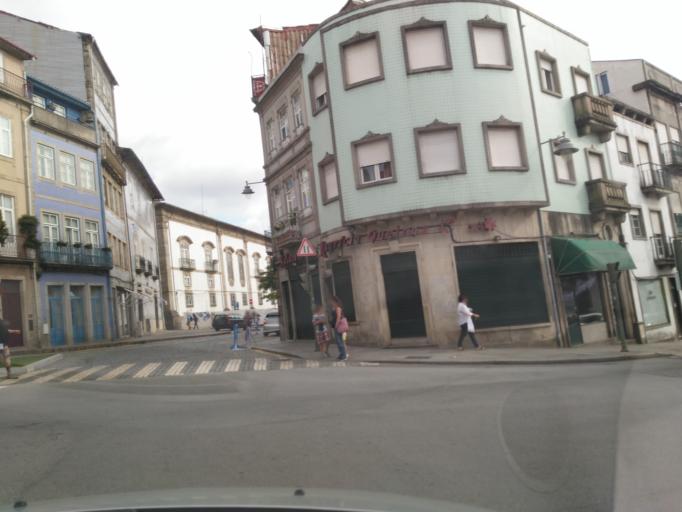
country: PT
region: Braga
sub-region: Braga
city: Braga
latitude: 41.5516
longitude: -8.4290
